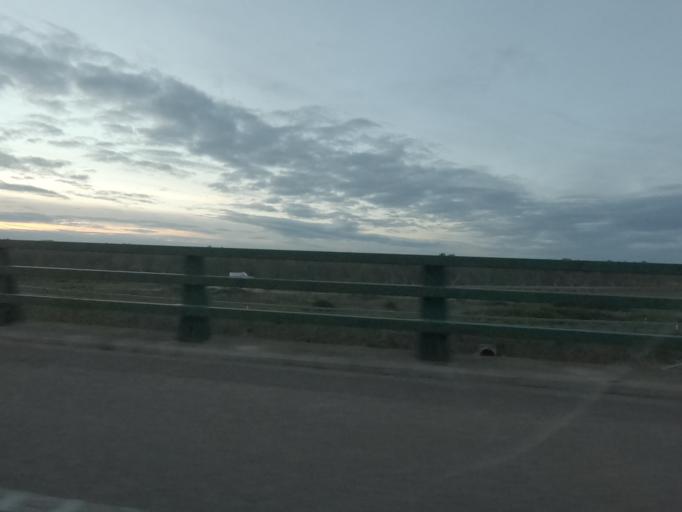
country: ES
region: Extremadura
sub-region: Provincia de Badajoz
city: Badajoz
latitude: 38.9238
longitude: -6.9423
